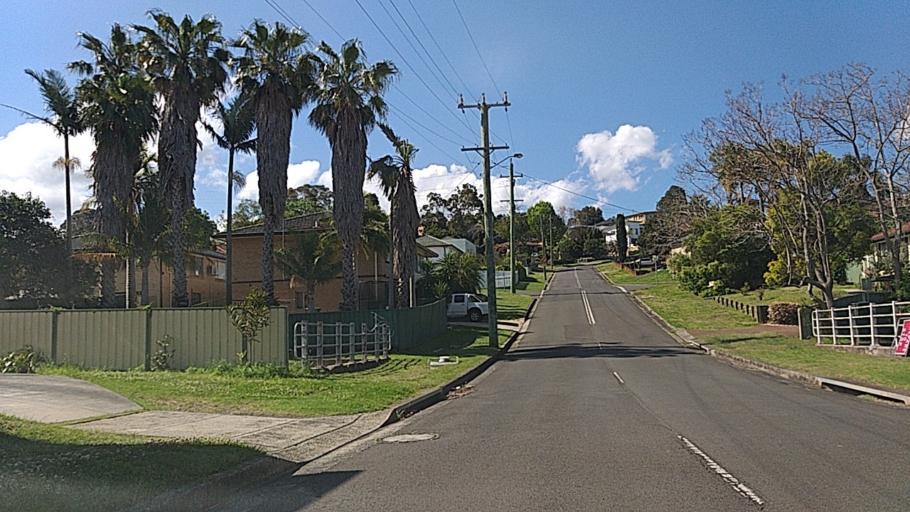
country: AU
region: New South Wales
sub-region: Wollongong
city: Cordeaux Heights
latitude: -34.4547
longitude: 150.8339
